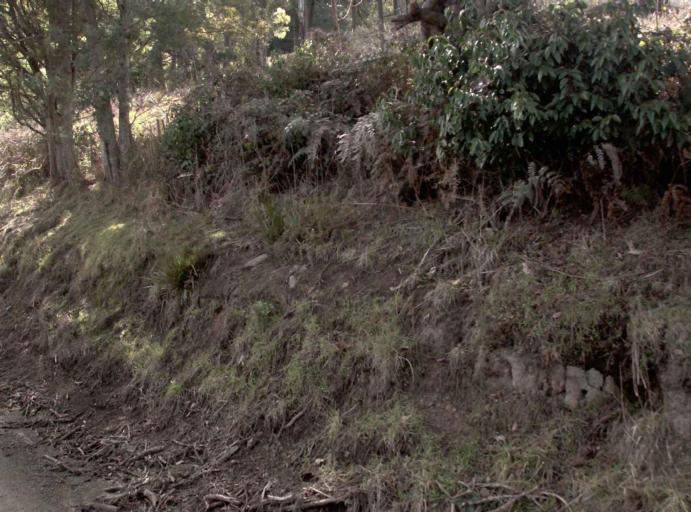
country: AU
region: Tasmania
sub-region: Launceston
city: Mayfield
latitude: -41.2456
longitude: 147.2464
